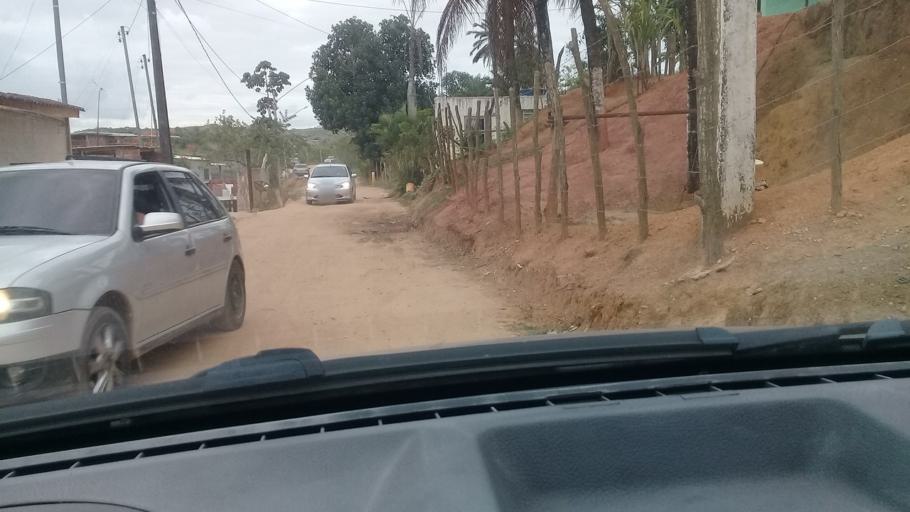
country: BR
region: Pernambuco
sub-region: Jaboatao Dos Guararapes
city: Jaboatao dos Guararapes
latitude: -8.0872
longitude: -35.0308
